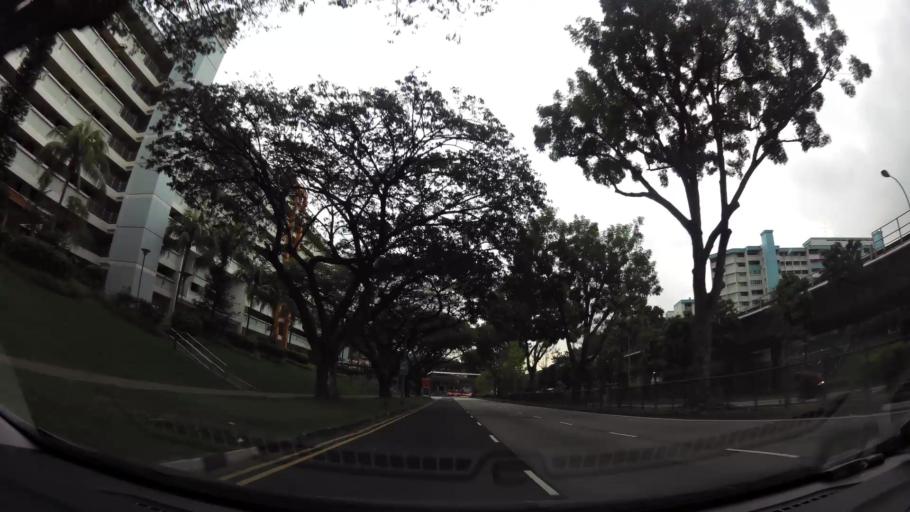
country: MY
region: Johor
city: Kampung Pasir Gudang Baru
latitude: 1.4338
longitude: 103.8349
